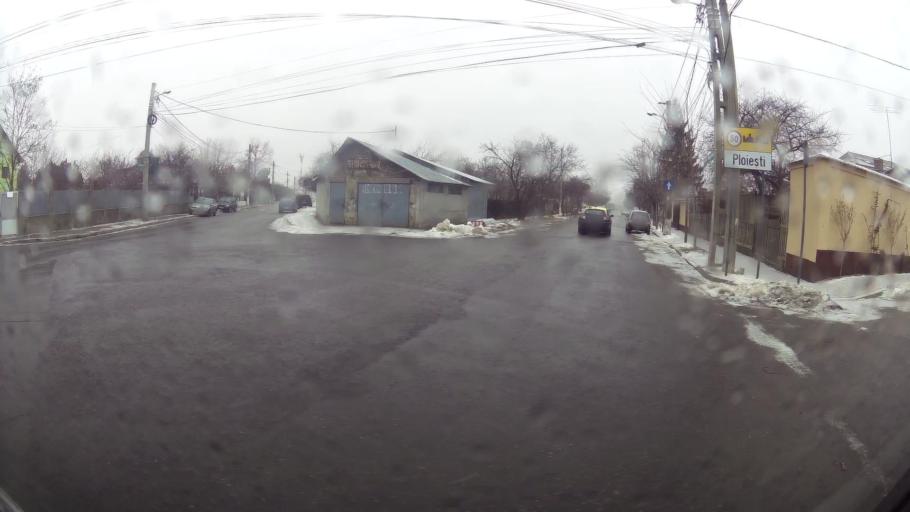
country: RO
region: Prahova
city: Ploiesti
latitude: 44.9568
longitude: 26.0391
